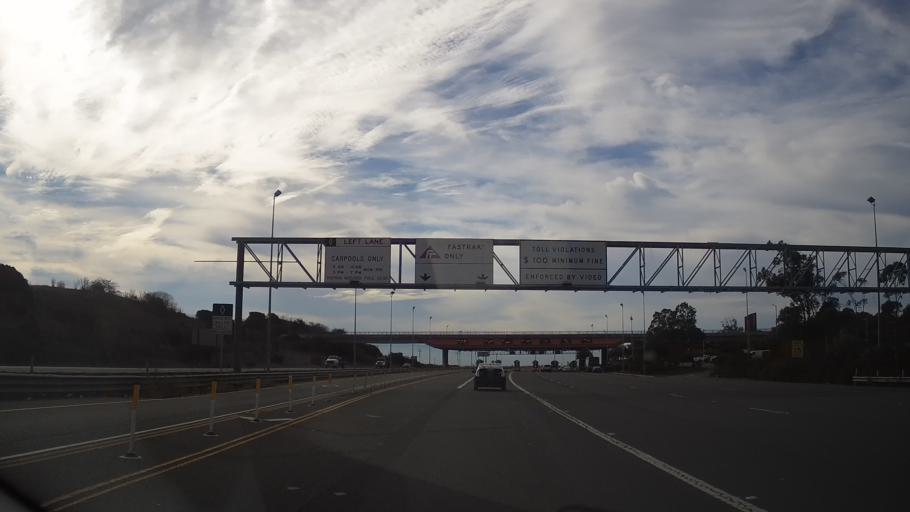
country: US
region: California
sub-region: Alameda County
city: Newark
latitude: 37.5365
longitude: -122.0730
